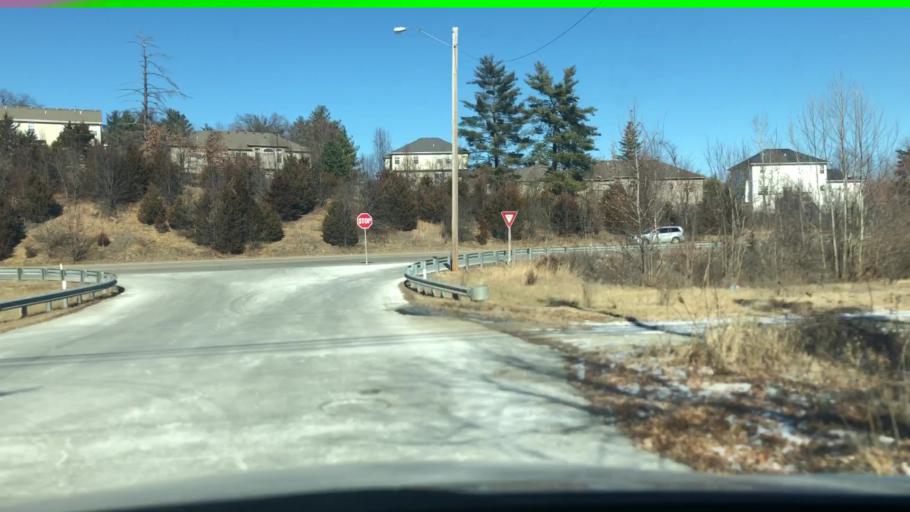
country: US
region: Missouri
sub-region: Boone County
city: Columbia
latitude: 38.9553
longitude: -92.3939
